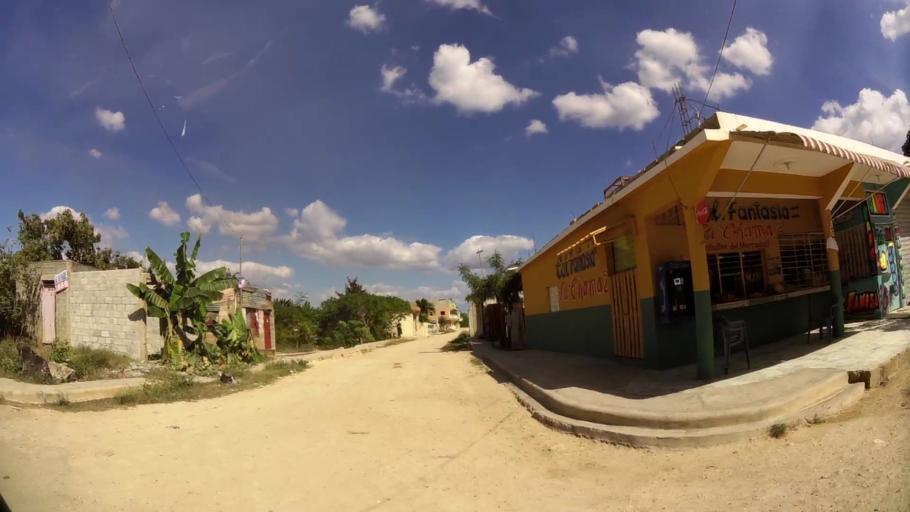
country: DO
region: Santo Domingo
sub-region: Santo Domingo
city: Santo Domingo Este
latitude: 18.4705
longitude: -69.7670
